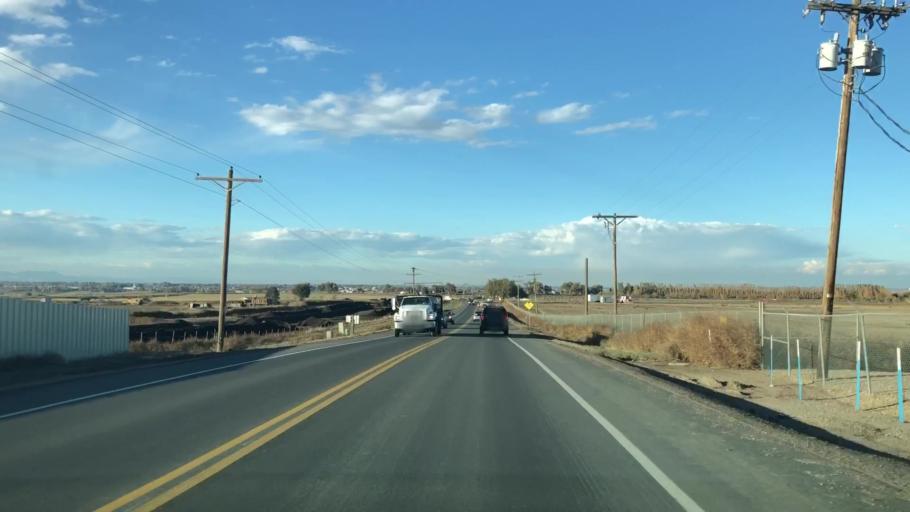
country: US
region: Colorado
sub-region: Larimer County
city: Loveland
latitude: 40.4612
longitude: -105.0204
